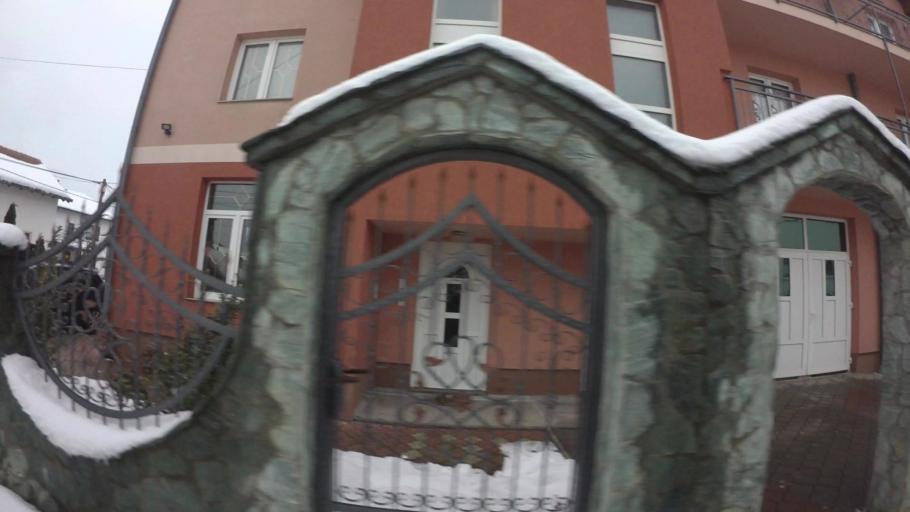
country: BA
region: Federation of Bosnia and Herzegovina
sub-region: Kanton Sarajevo
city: Sarajevo
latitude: 43.8429
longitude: 18.3135
